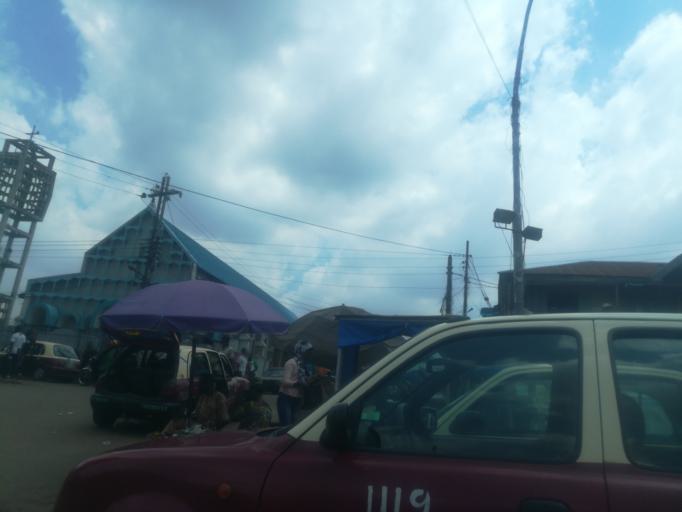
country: NG
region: Oyo
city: Ibadan
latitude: 7.3870
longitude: 3.8860
